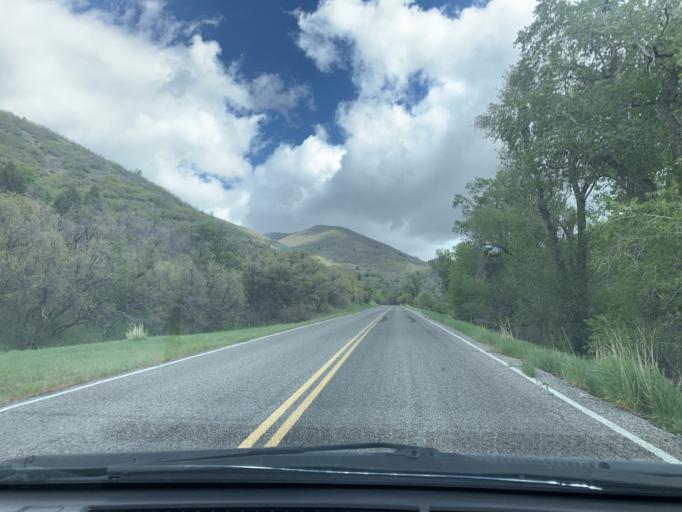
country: US
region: Utah
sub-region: Juab County
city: Nephi
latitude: 39.7683
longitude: -111.7057
